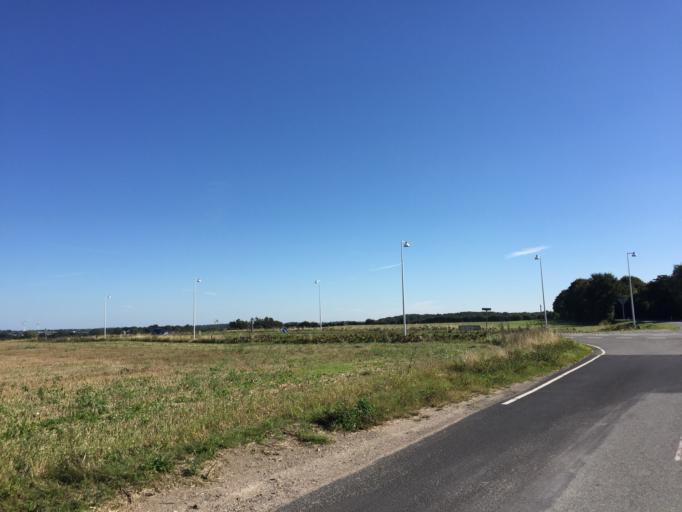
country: DK
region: South Denmark
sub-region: Assens Kommune
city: Assens
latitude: 55.2965
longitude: 9.9379
